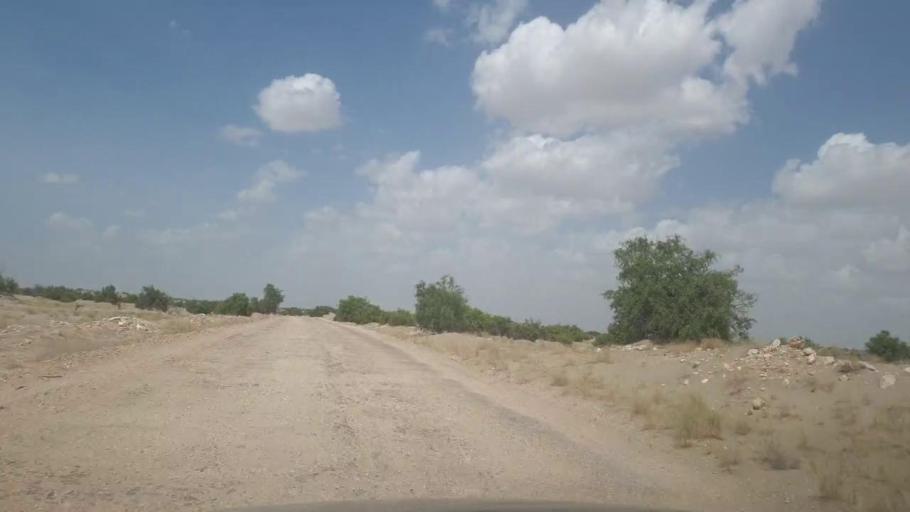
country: PK
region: Sindh
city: Kot Diji
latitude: 27.2633
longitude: 69.1752
